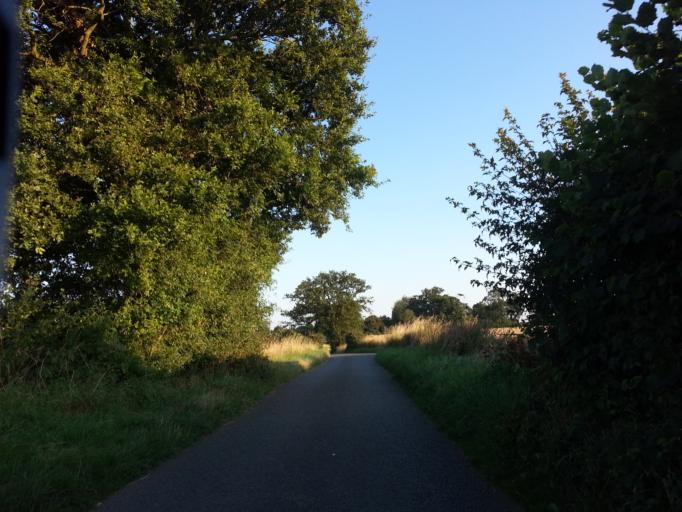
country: GB
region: England
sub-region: Suffolk
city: Kesgrave
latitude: 52.1112
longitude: 1.2341
